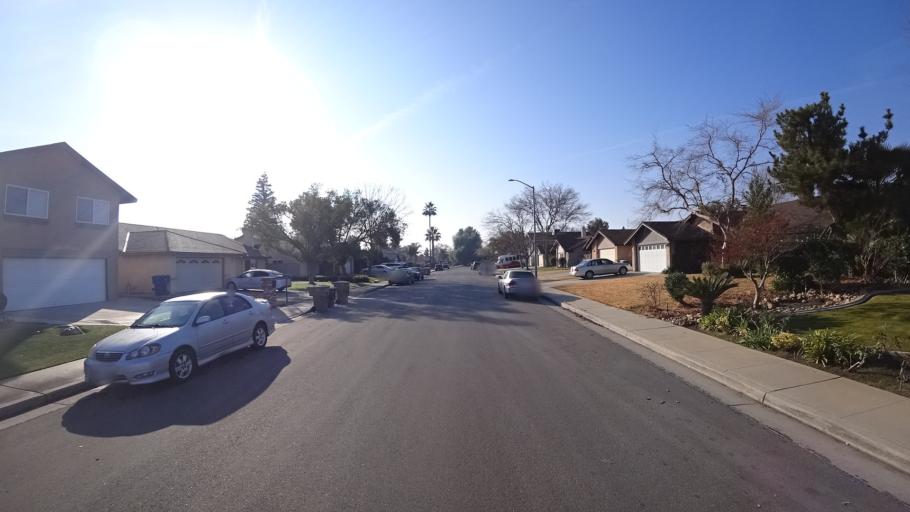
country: US
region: California
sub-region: Kern County
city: Oildale
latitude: 35.4052
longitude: -118.9335
